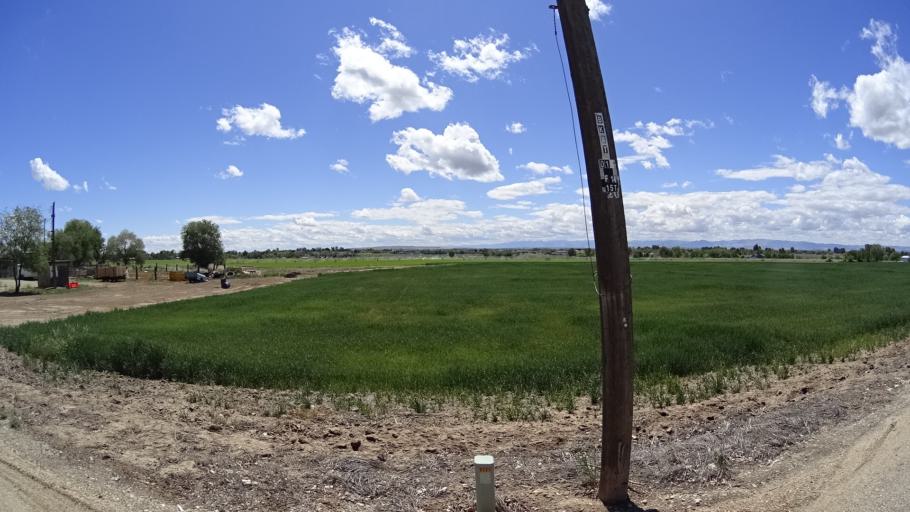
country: US
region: Idaho
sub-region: Ada County
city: Meridian
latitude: 43.5903
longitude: -116.4653
